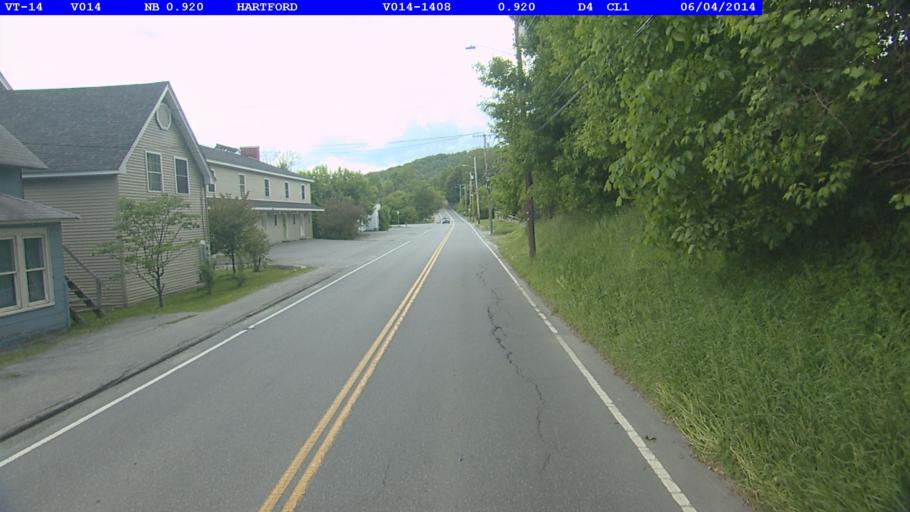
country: US
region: Vermont
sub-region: Windsor County
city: White River Junction
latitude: 43.6588
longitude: -72.3351
